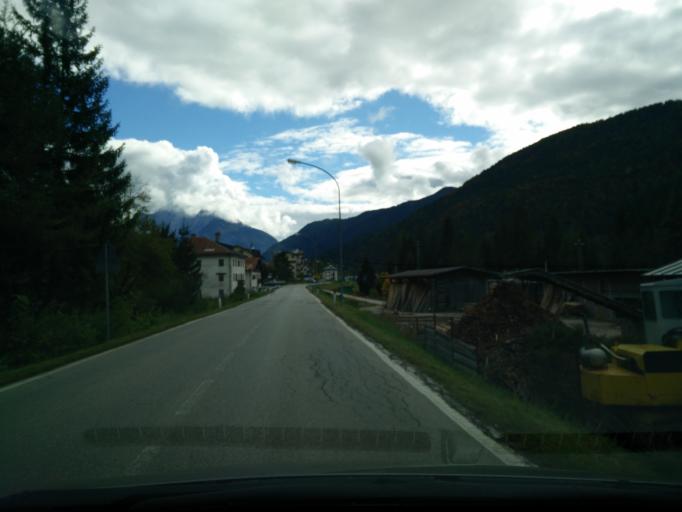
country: IT
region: Veneto
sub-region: Provincia di Belluno
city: Auronzo
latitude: 46.5717
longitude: 12.3977
